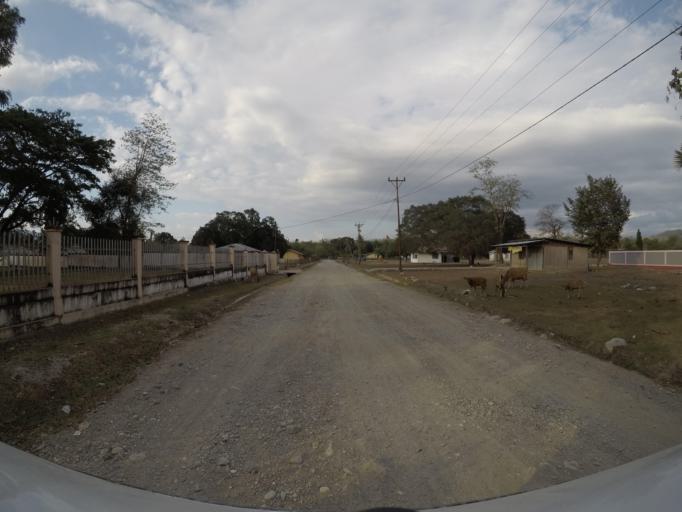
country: TL
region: Bobonaro
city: Maliana
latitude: -8.8812
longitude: 125.2106
